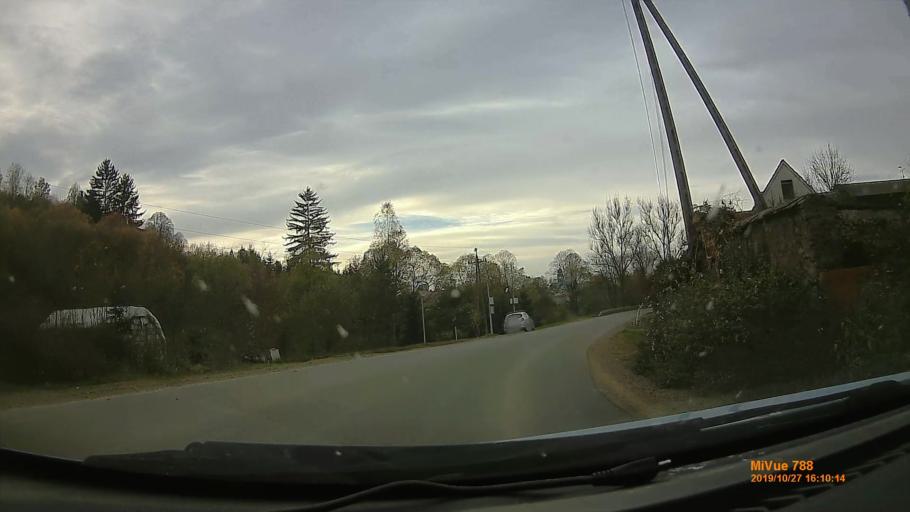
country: PL
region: Lower Silesian Voivodeship
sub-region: Powiat klodzki
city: Radkow
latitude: 50.5520
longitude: 16.4371
